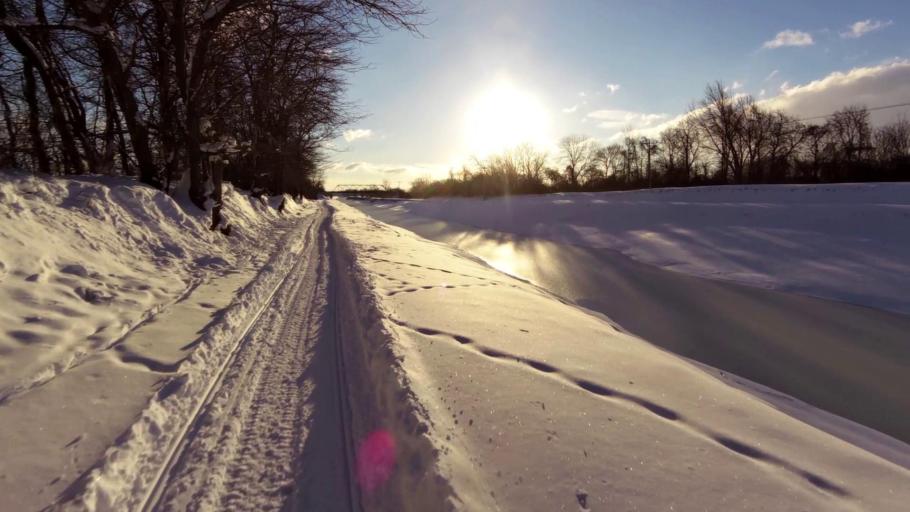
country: US
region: New York
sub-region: Orleans County
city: Medina
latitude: 43.2332
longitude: -78.3601
